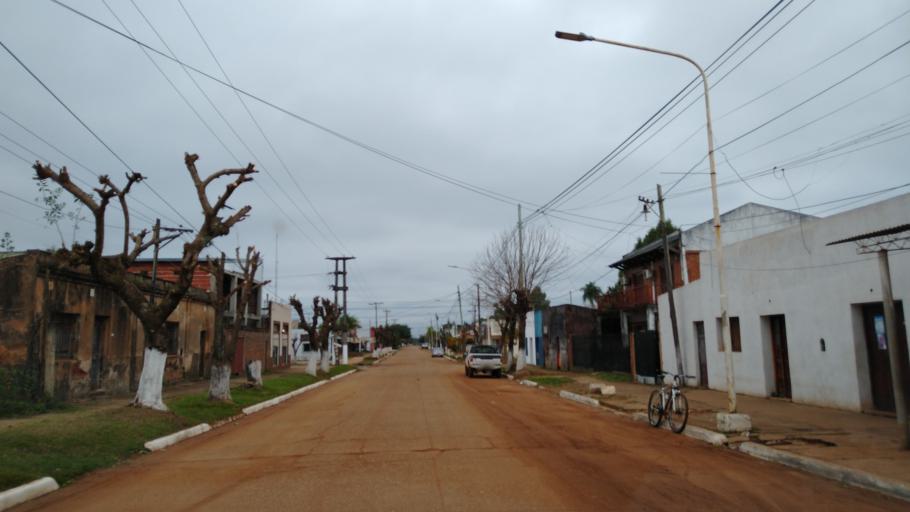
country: AR
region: Corrientes
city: Alvear
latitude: -29.0920
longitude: -56.5473
